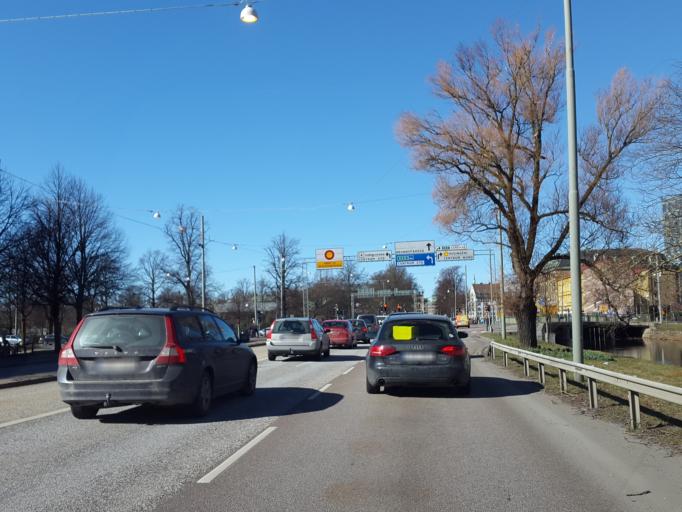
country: SE
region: Vaestra Goetaland
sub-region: Goteborg
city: Goeteborg
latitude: 57.7075
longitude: 11.9800
